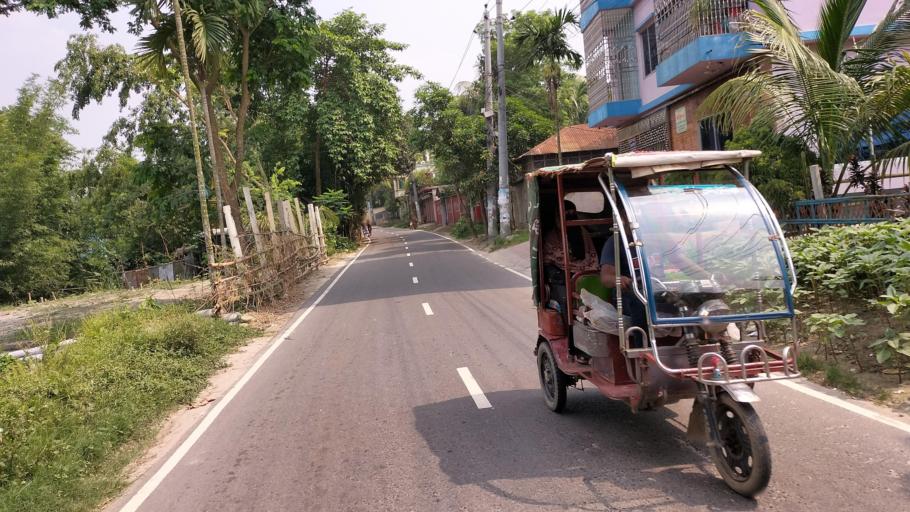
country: BD
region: Dhaka
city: Azimpur
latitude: 23.7014
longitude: 90.2917
